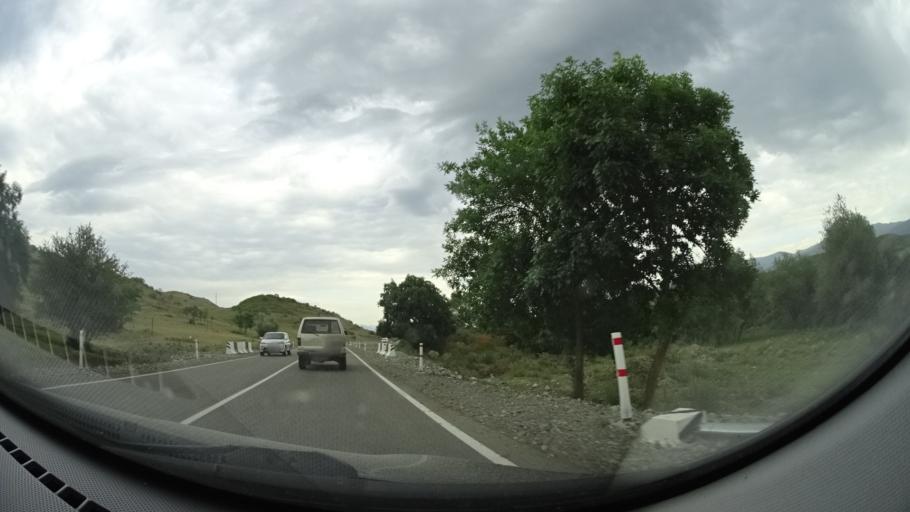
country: GE
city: Vale
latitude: 41.6496
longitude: 42.8628
